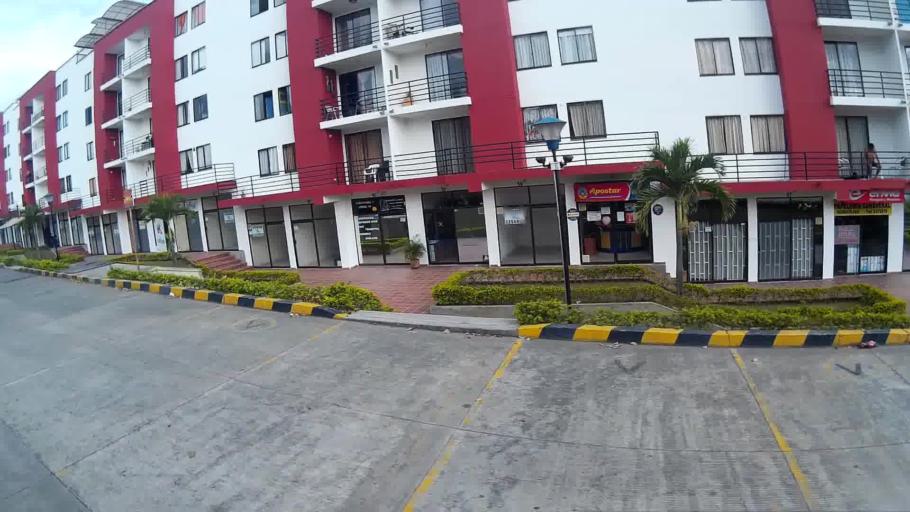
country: CO
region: Risaralda
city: Pereira
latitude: 4.8114
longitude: -75.7380
